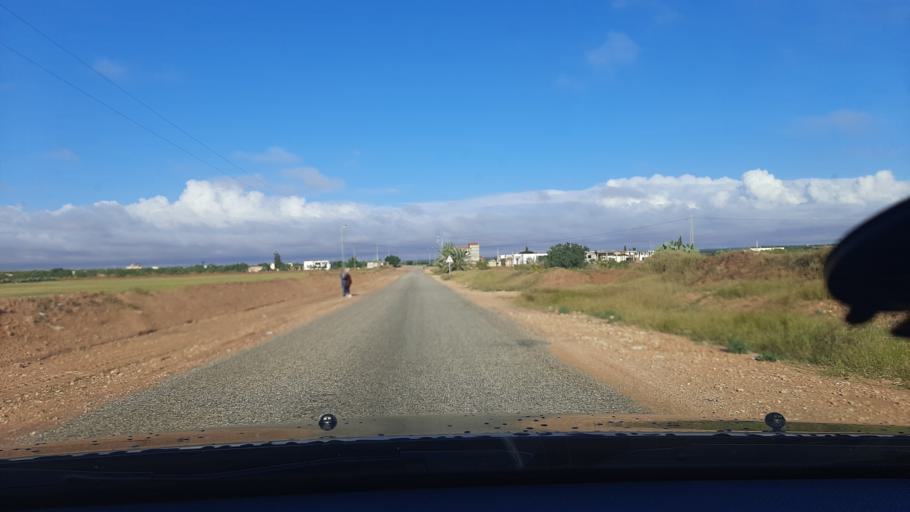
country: TN
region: Safaqis
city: Sfax
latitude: 34.8841
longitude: 10.6287
